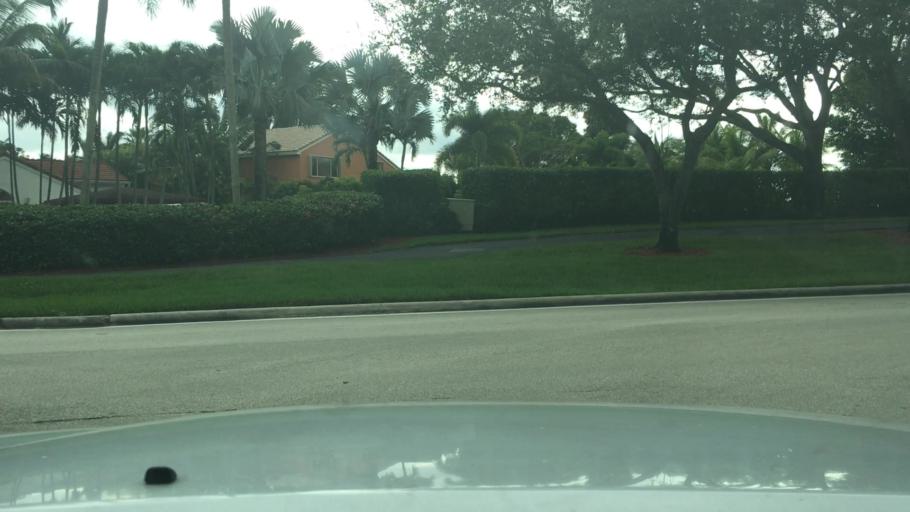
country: US
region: Florida
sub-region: Broward County
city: Sunshine Ranches
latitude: 26.0025
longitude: -80.3667
